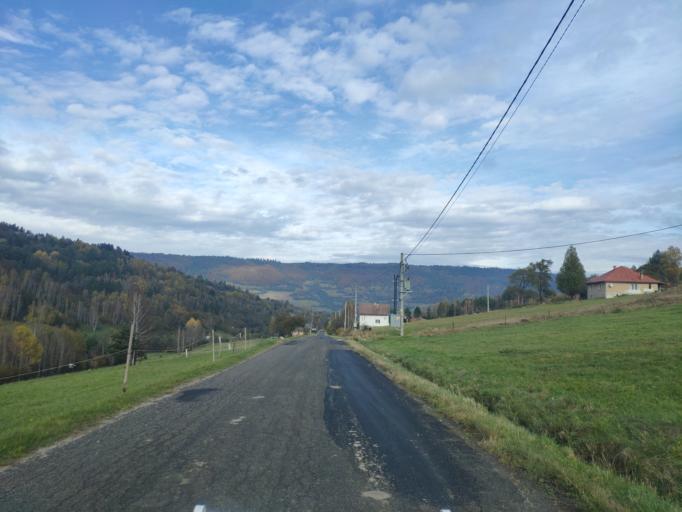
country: SK
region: Kosicky
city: Spisska Nova Ves
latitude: 48.8240
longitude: 20.6244
